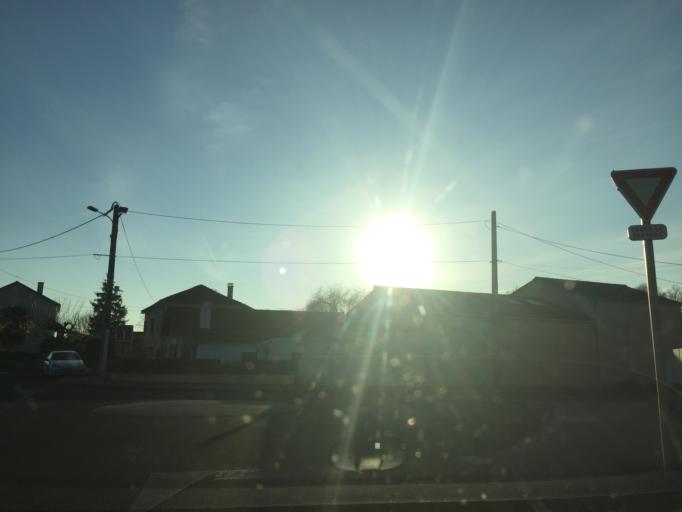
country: FR
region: Poitou-Charentes
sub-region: Departement de la Charente
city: Chalais
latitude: 45.2688
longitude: 0.0425
